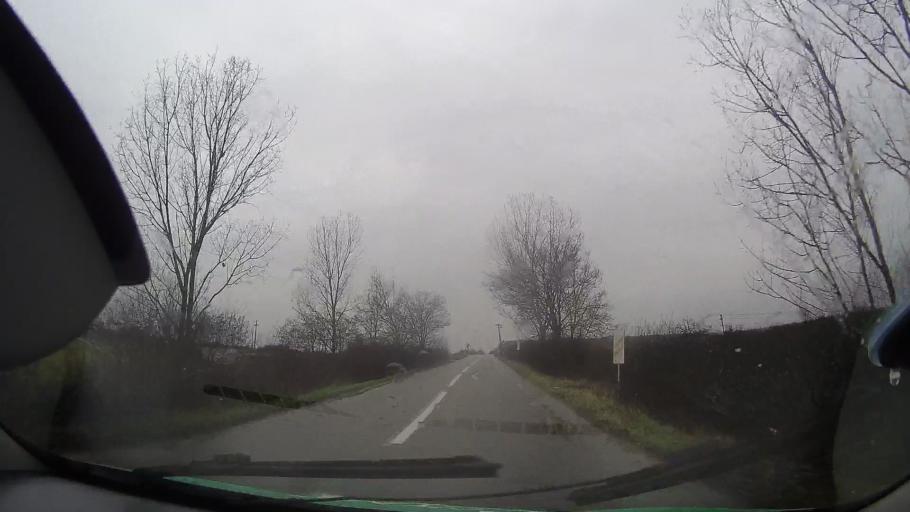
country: RO
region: Bihor
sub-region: Comuna Tinca
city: Gurbediu
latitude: 46.7722
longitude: 21.8949
